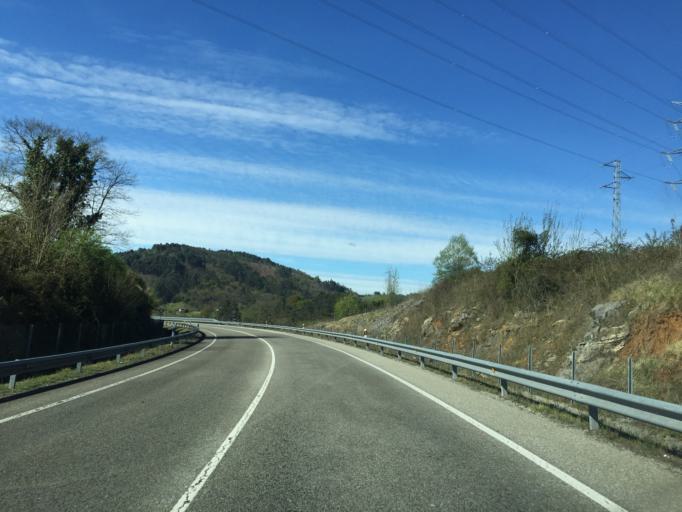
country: ES
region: Asturias
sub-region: Province of Asturias
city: Llanera
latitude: 43.3658
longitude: -5.9579
